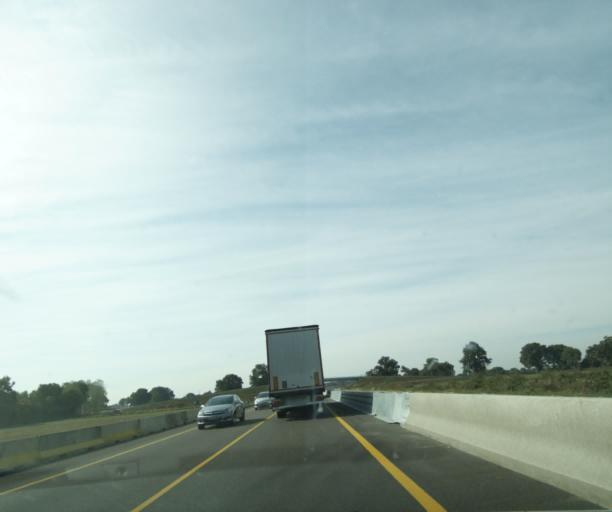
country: FR
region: Bourgogne
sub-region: Departement de Saone-et-Loire
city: Paray-le-Monial
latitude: 46.4832
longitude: 4.1486
